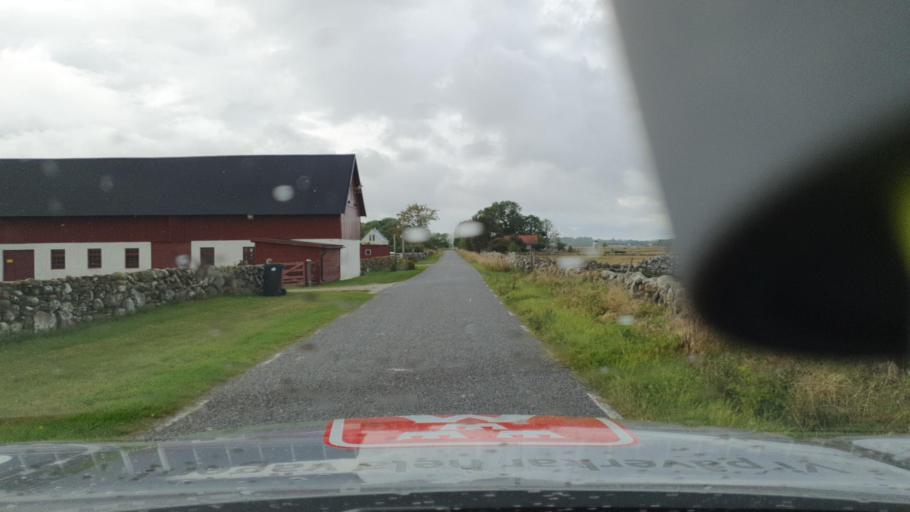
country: SE
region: Gotland
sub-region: Gotland
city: Hemse
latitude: 57.0017
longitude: 18.3488
